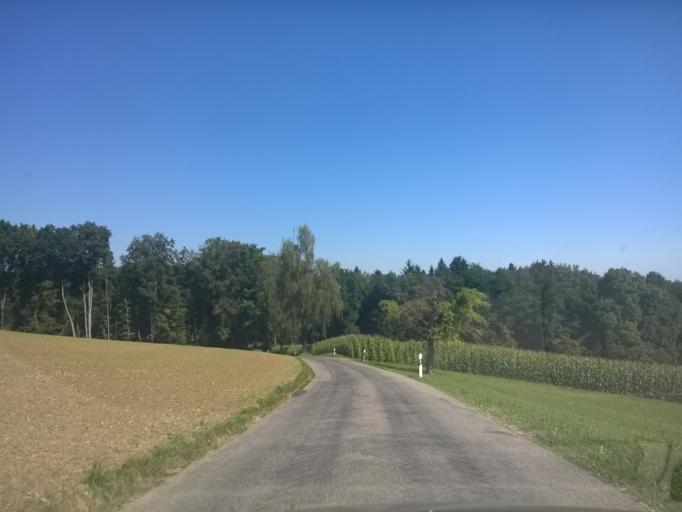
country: CH
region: Zurich
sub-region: Bezirk Winterthur
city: Wuelflingen (Kreis 6) / Niederfeld
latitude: 47.4957
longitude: 8.6659
